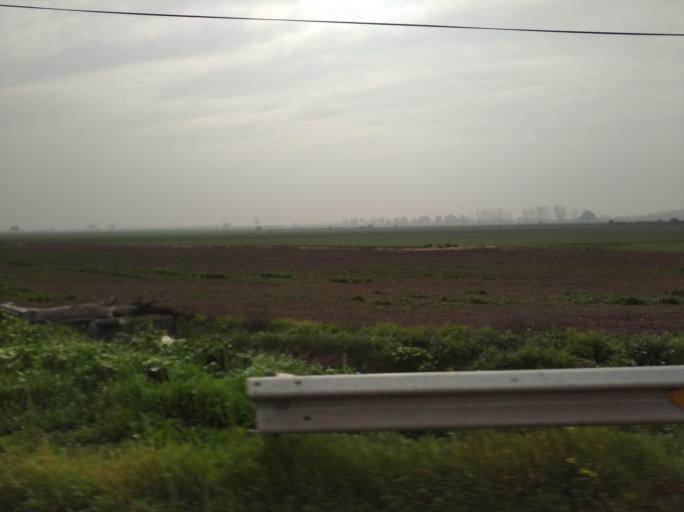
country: CL
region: Santiago Metropolitan
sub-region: Provincia de Chacabuco
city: Lampa
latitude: -33.3438
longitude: -70.8101
